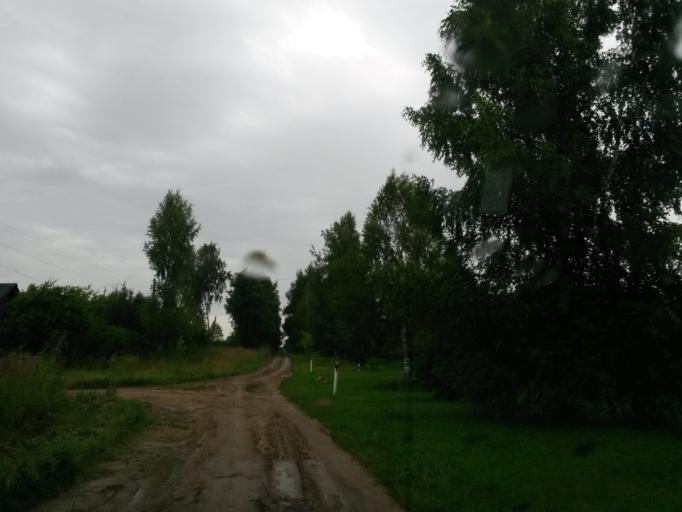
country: RU
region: Jaroslavl
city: Tutayev
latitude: 57.9452
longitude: 39.4417
